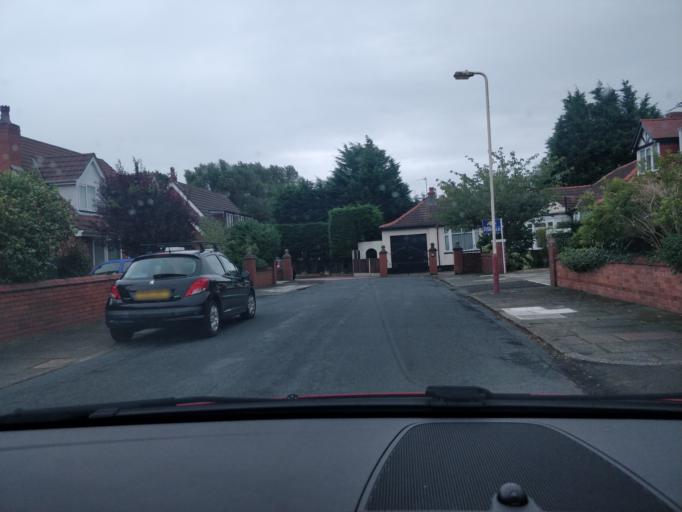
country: GB
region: England
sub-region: Sefton
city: Southport
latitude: 53.6359
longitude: -2.9857
